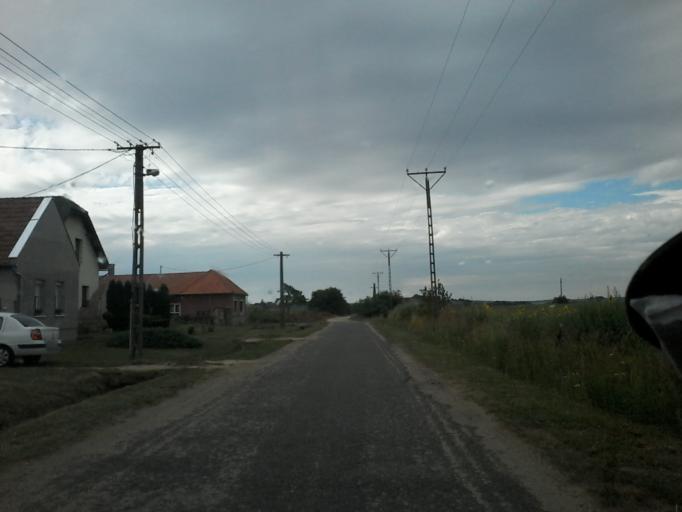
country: HU
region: Vas
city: Celldomolk
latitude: 47.2113
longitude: 17.0577
